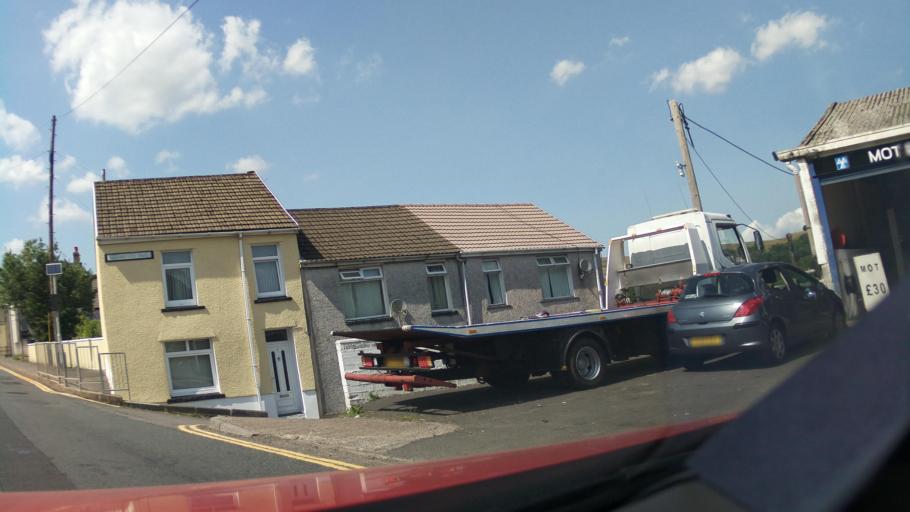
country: GB
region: Wales
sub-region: Caerphilly County Borough
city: Rhymney
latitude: 51.7418
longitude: -3.2767
